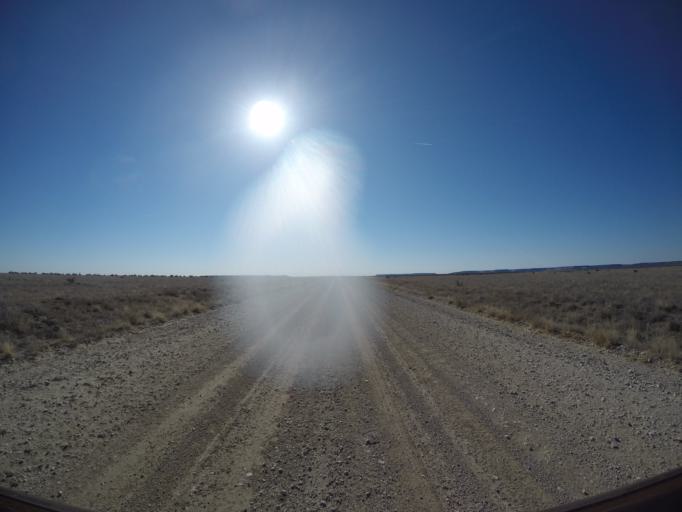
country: US
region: Colorado
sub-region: Otero County
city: La Junta
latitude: 37.6705
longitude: -103.6203
